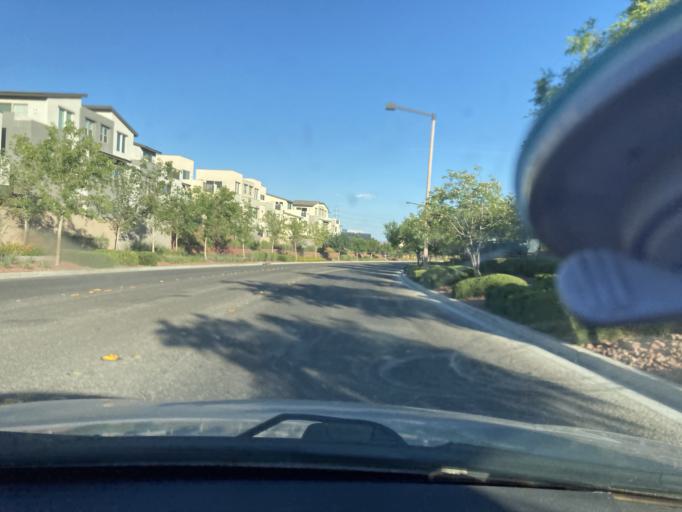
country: US
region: Nevada
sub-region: Clark County
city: Summerlin South
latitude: 36.1558
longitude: -115.3419
